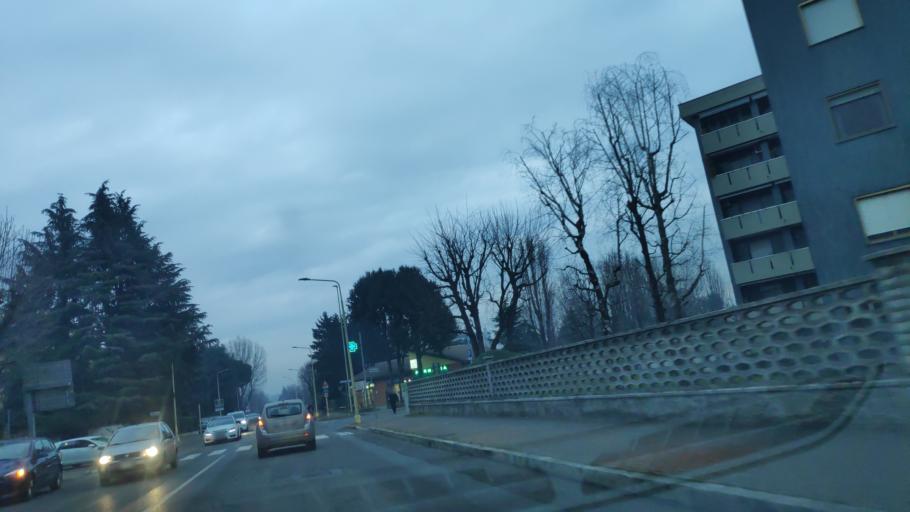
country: IT
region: Lombardy
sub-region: Citta metropolitana di Milano
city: Corsico
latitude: 45.4214
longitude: 9.1203
